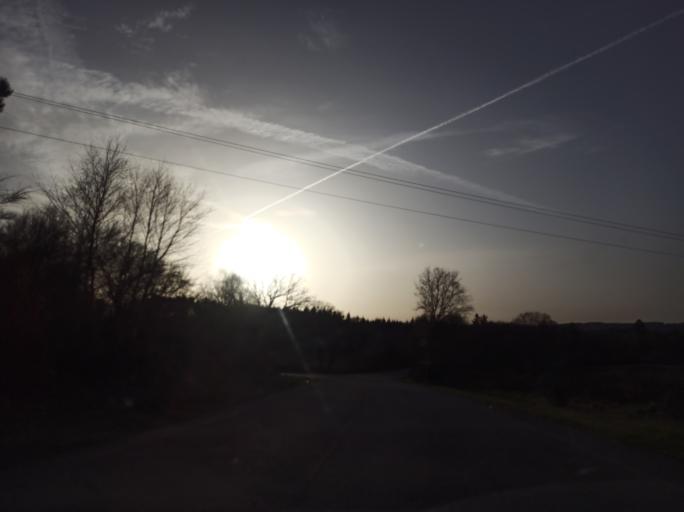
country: ES
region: Galicia
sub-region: Provincia de Lugo
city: Friol
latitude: 43.0228
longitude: -7.8339
